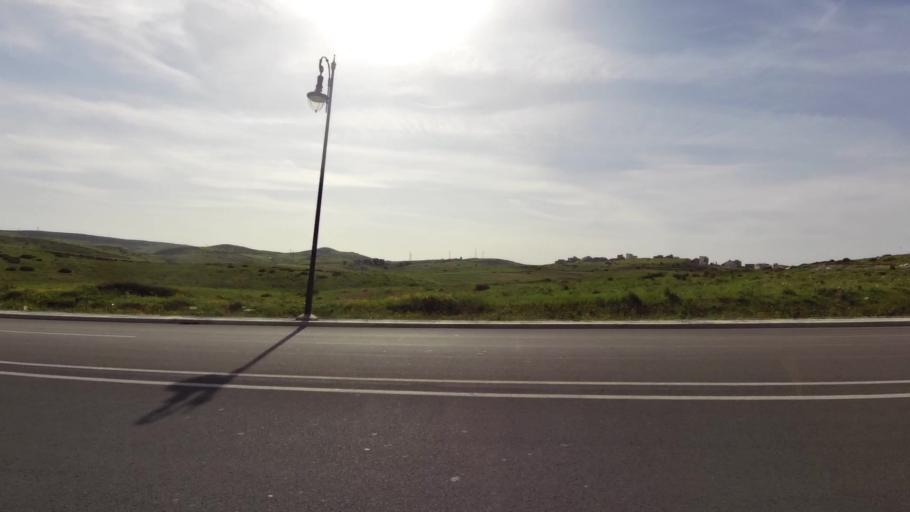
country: MA
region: Tanger-Tetouan
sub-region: Tanger-Assilah
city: Tangier
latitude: 35.7092
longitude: -5.7803
